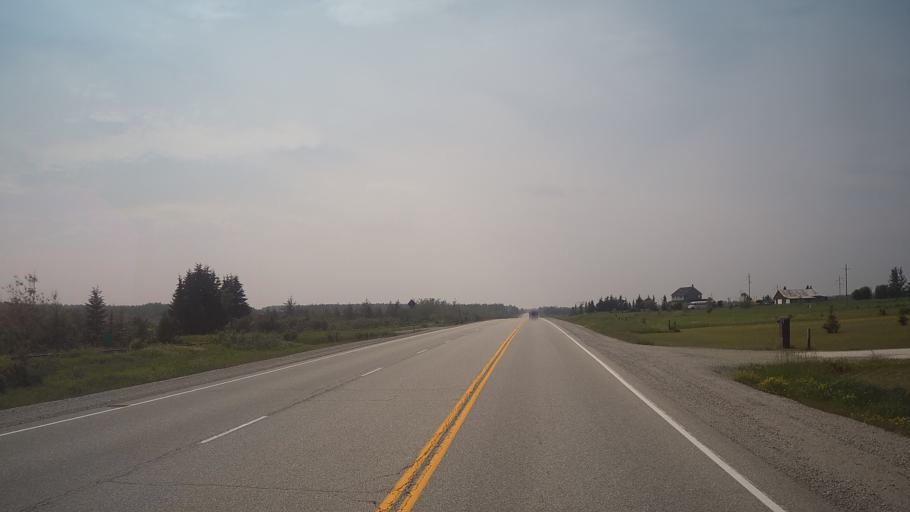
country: CA
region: Ontario
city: Kapuskasing
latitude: 49.3344
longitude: -82.0912
